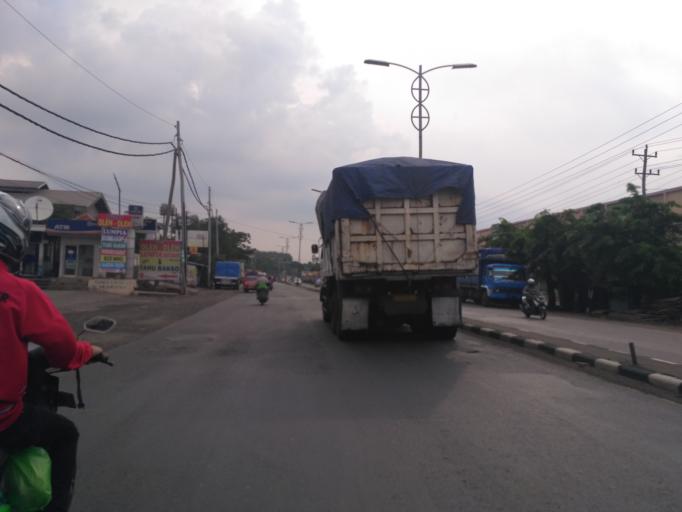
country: ID
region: Central Java
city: Semarang
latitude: -6.9758
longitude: 110.3213
